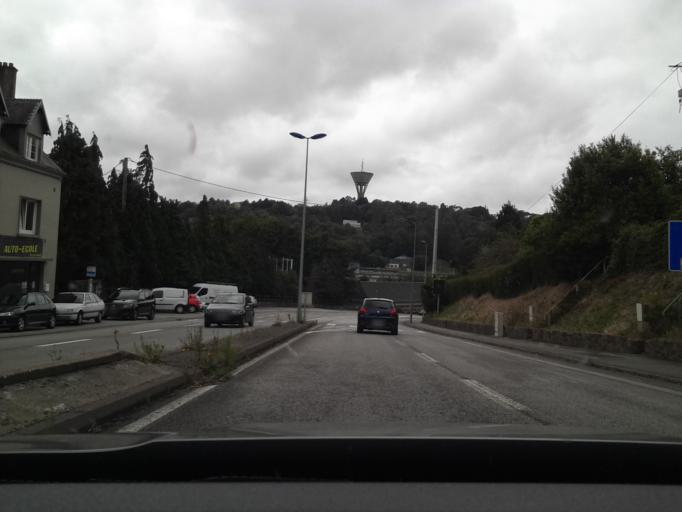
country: FR
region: Lower Normandy
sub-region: Departement de la Manche
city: Cherbourg-Octeville
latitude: 49.6235
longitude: -1.6133
